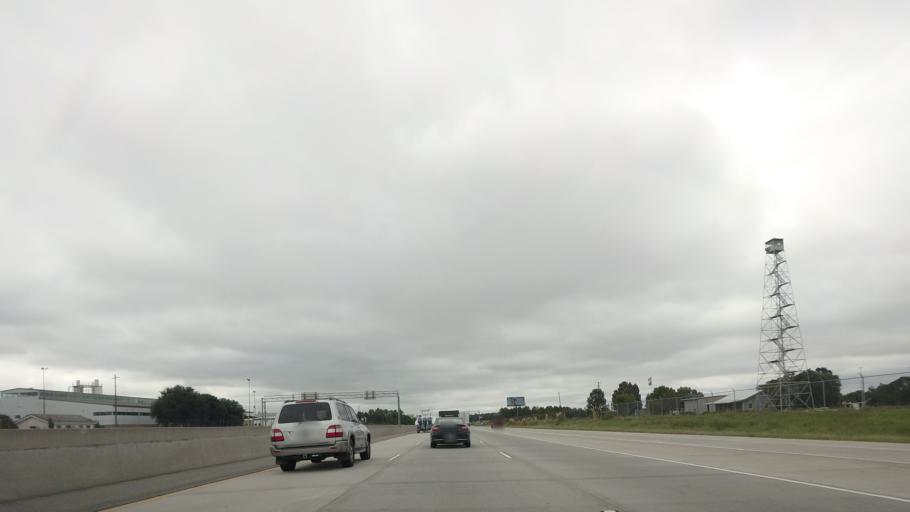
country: US
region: Georgia
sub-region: Cook County
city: Adel
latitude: 31.1102
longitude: -83.4267
